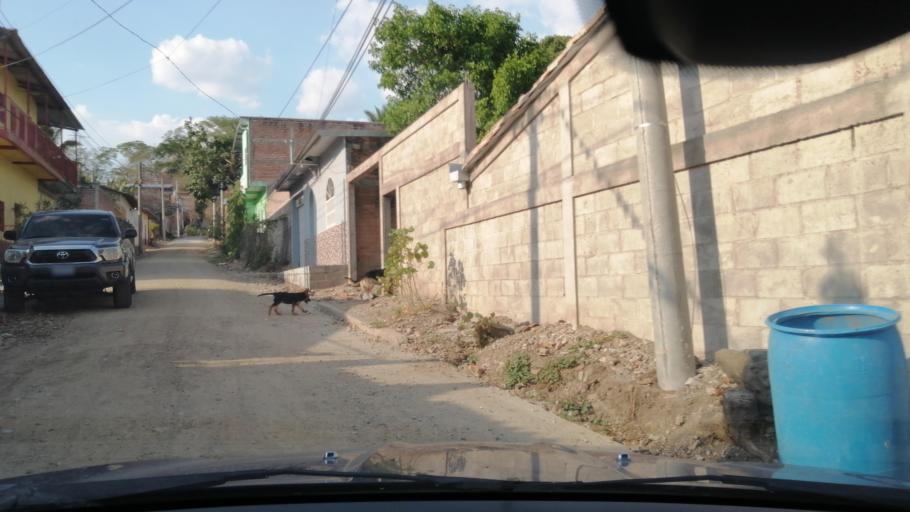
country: SV
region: Santa Ana
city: Metapan
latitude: 14.3282
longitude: -89.4291
